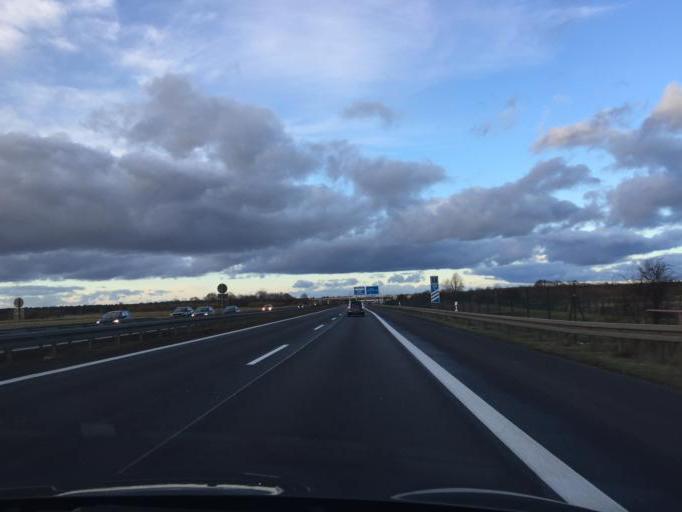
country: DE
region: Brandenburg
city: Mittenwalde
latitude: 52.3081
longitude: 13.5558
